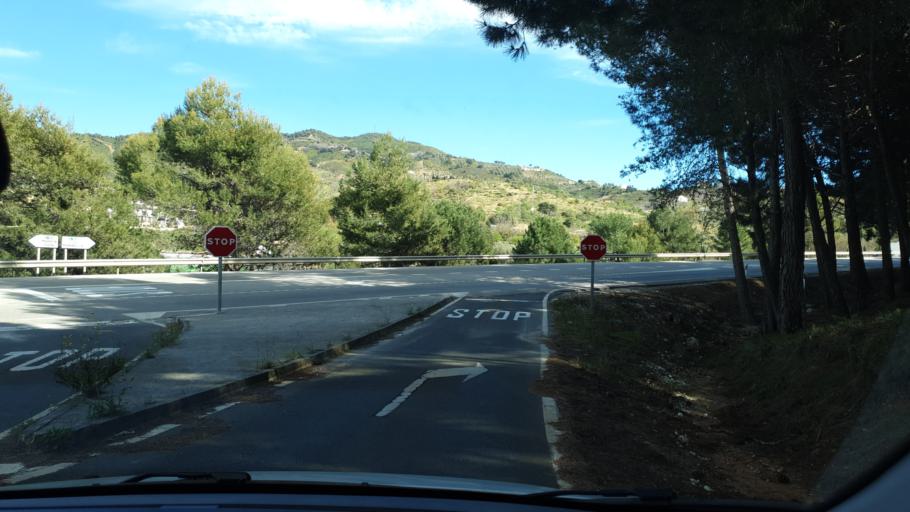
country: ES
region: Andalusia
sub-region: Provincia de Malaga
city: Ojen
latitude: 36.5915
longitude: -4.8525
